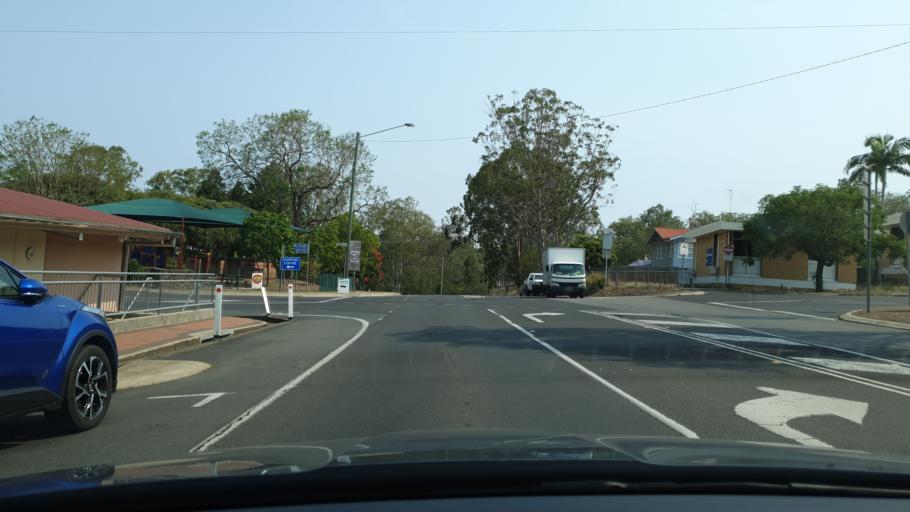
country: AU
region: Queensland
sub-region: Ipswich
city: Deebing Heights
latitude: -27.9985
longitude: 152.6815
